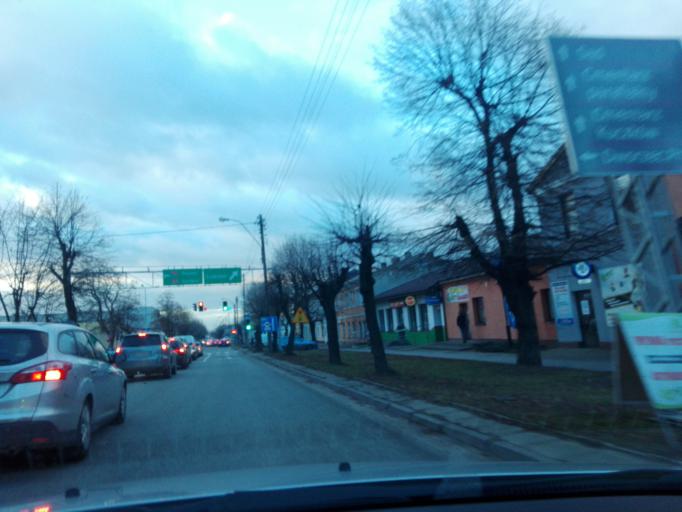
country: PL
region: Lodz Voivodeship
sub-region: Powiat kutnowski
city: Kutno
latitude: 52.2340
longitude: 19.3553
